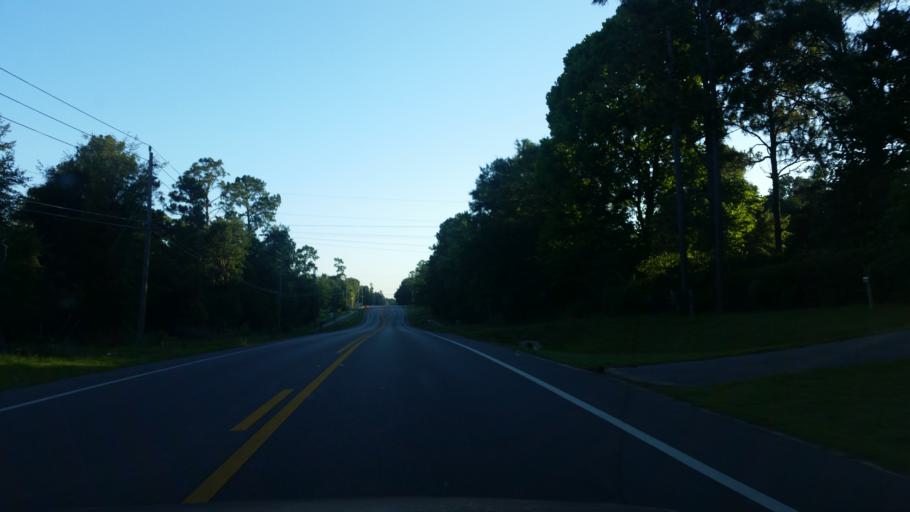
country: US
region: Florida
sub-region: Escambia County
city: Cantonment
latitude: 30.5857
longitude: -87.3282
